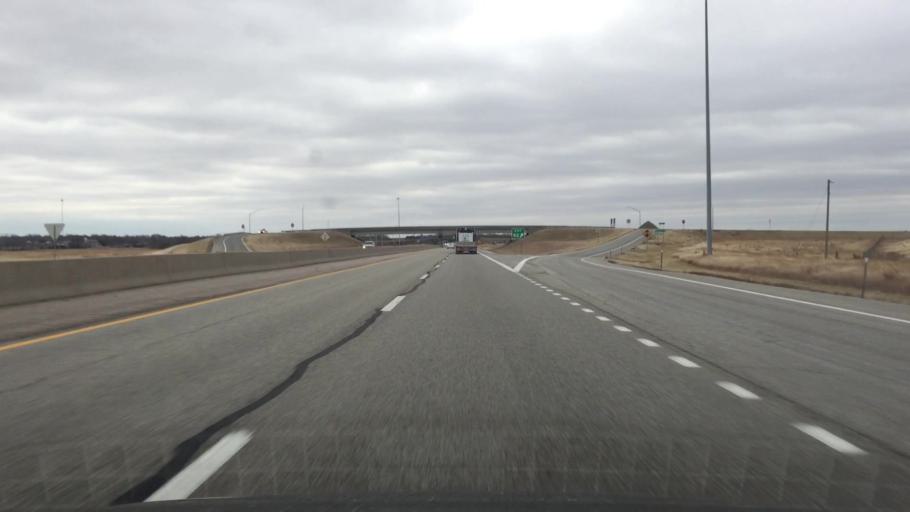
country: US
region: Kansas
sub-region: Butler County
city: El Dorado
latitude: 38.0529
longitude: -96.6316
